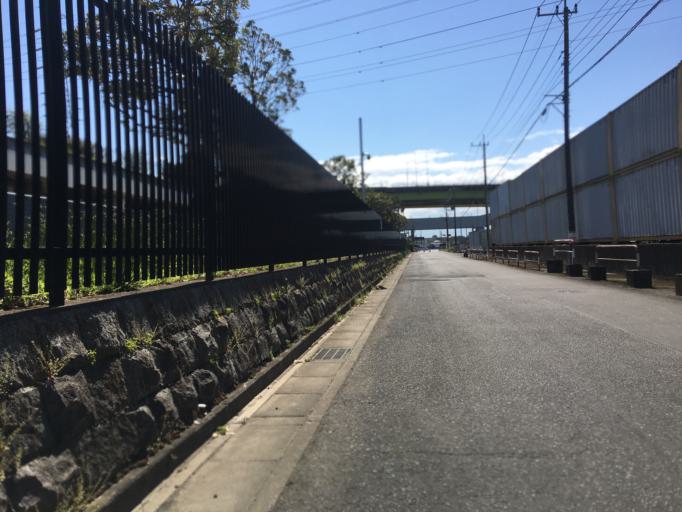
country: JP
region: Saitama
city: Wako
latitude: 35.8035
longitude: 139.6192
